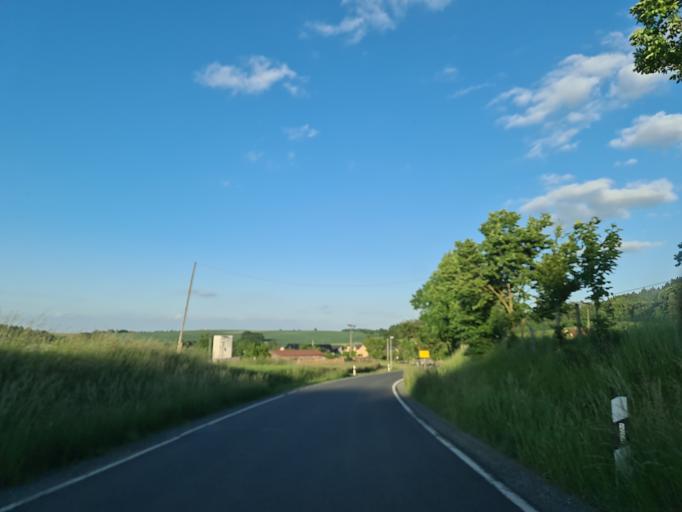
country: DE
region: Saxony
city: Reuth
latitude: 50.4667
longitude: 11.9967
